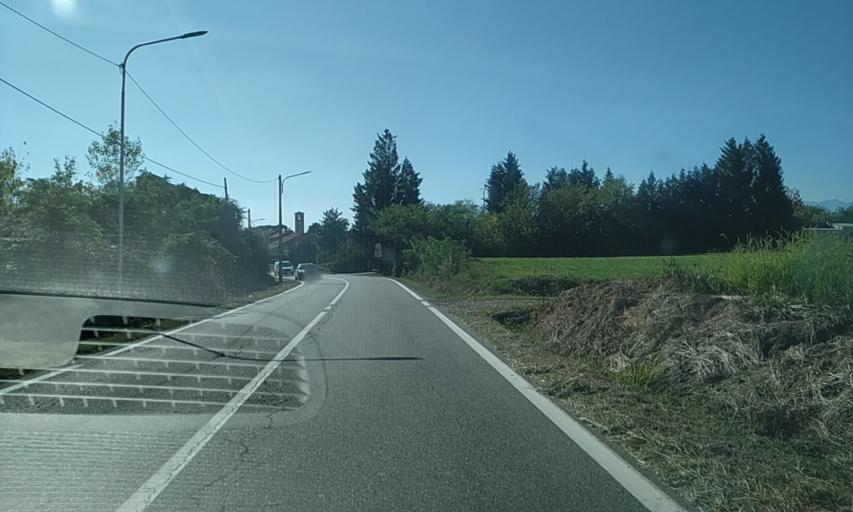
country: IT
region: Piedmont
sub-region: Provincia di Vercelli
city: San Giacomo Vercellese
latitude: 45.4985
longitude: 8.3304
